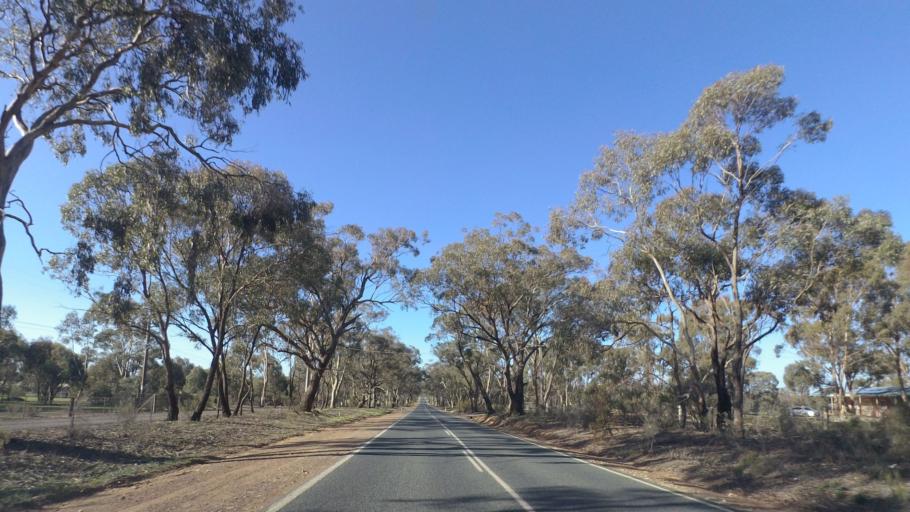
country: AU
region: Victoria
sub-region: Greater Bendigo
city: Epsom
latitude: -36.6765
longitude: 144.3902
